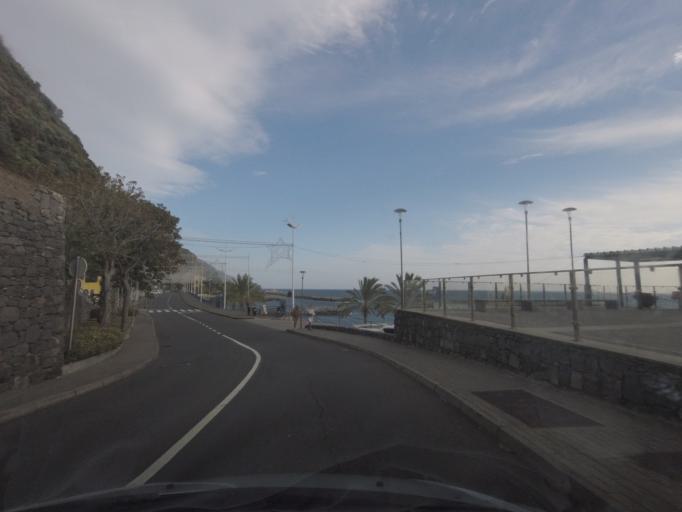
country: PT
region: Madeira
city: Calheta
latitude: 32.7210
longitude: -17.1783
